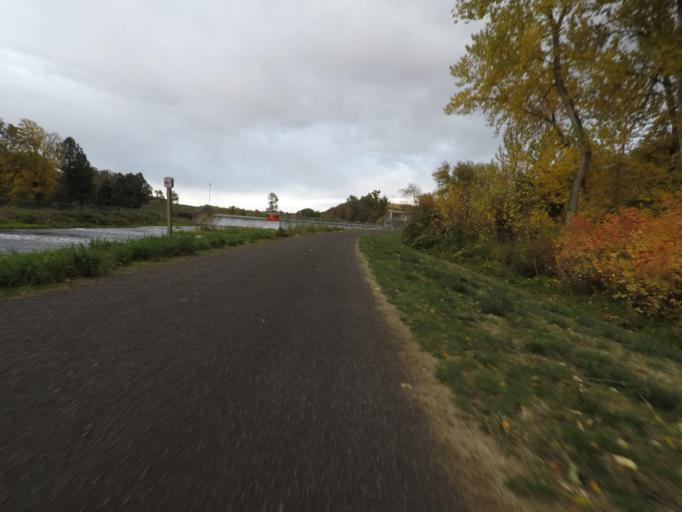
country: US
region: Washington
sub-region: Walla Walla County
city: Walla Walla East
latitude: 46.0798
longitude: -118.2562
